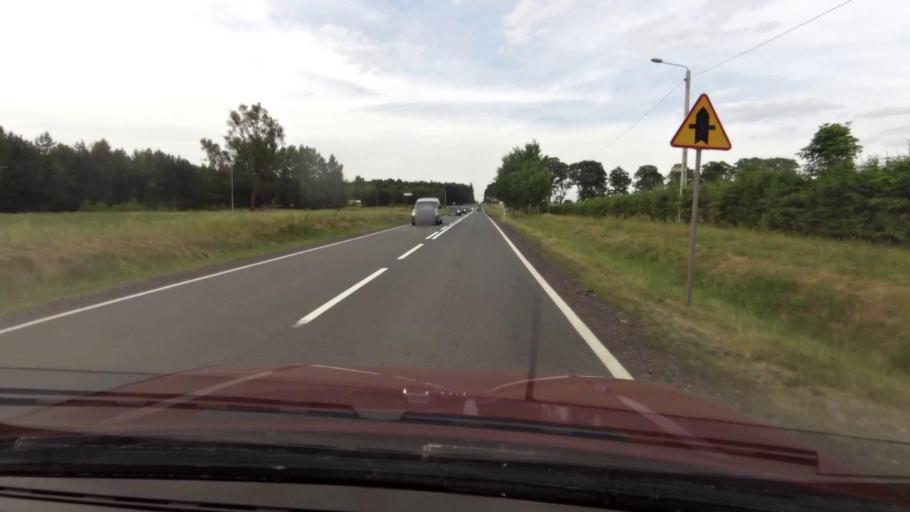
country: PL
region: Pomeranian Voivodeship
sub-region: Powiat bytowski
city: Trzebielino
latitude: 54.2390
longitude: 17.0932
